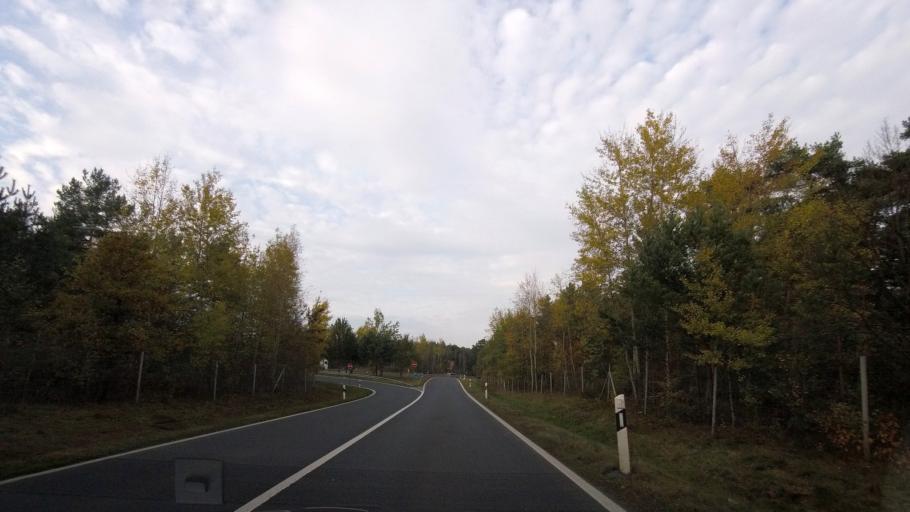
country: DE
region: Brandenburg
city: Borkheide
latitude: 52.2166
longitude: 12.9030
